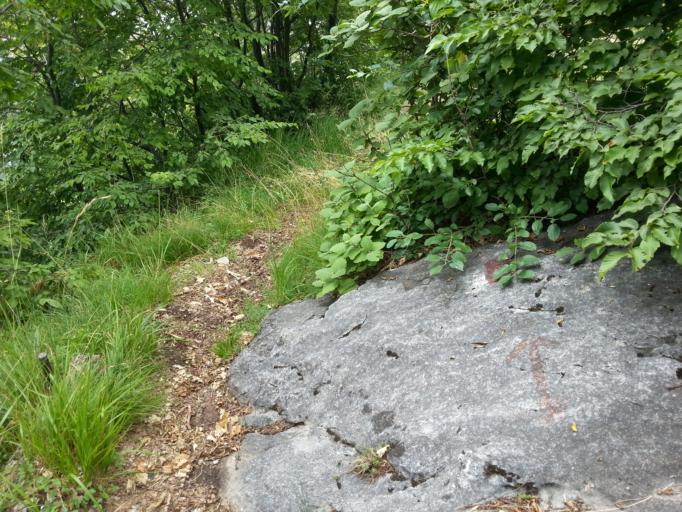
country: IT
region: Lombardy
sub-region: Provincia di Lecco
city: Ballabio
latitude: 45.8802
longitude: 9.4225
